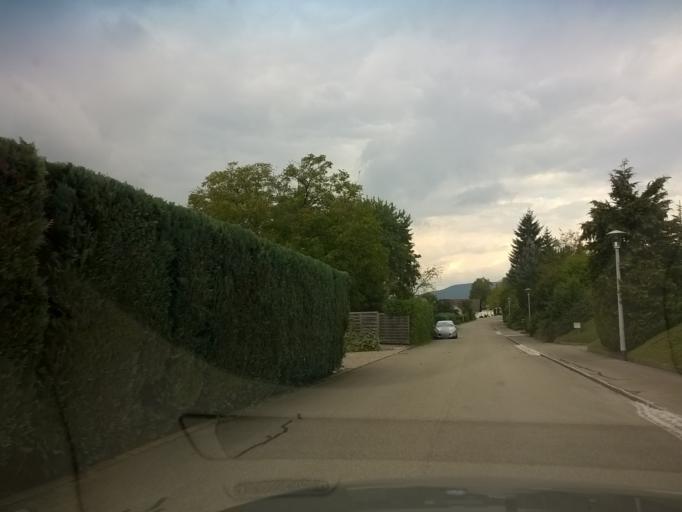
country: CH
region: Zurich
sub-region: Bezirk Buelach
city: Embrach / Embrach (Dorfkern)
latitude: 47.4998
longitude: 8.6062
